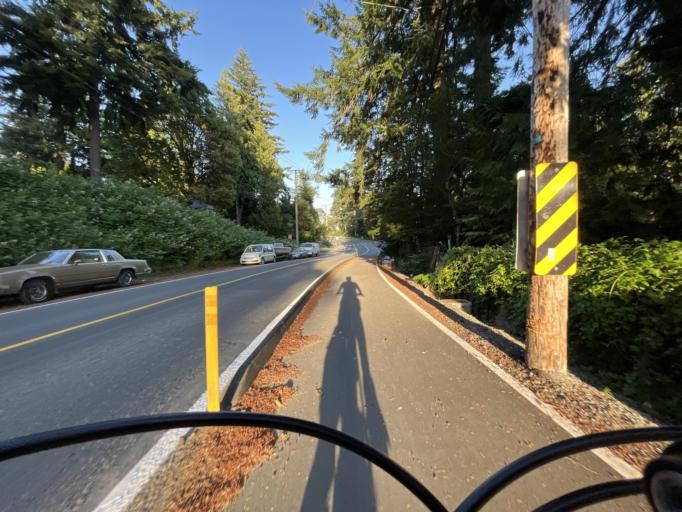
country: CA
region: British Columbia
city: Langford
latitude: 48.4495
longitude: -123.5235
